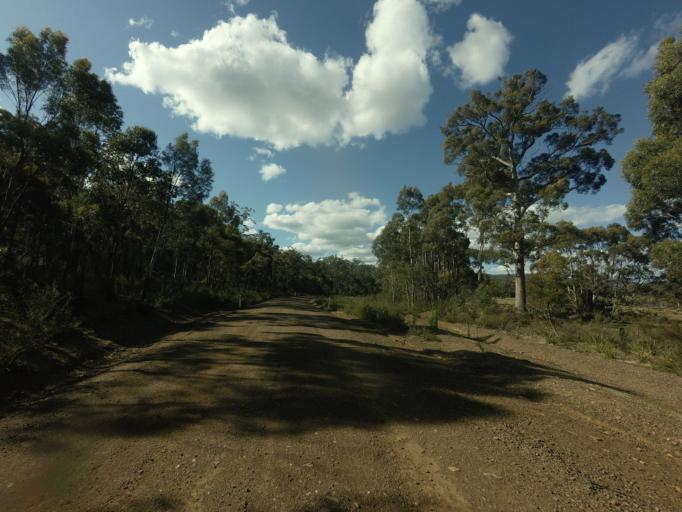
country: AU
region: Tasmania
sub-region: Break O'Day
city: St Helens
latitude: -41.8488
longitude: 148.0109
